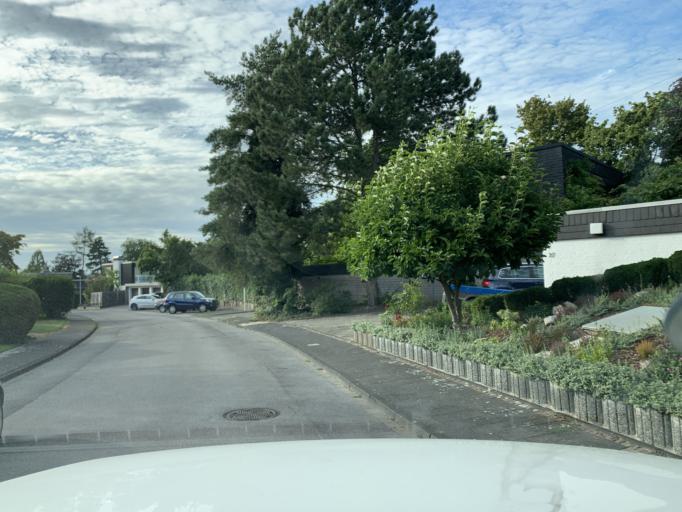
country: DE
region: North Rhine-Westphalia
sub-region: Regierungsbezirk Dusseldorf
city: Muelheim (Ruhr)
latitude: 51.4170
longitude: 6.8467
